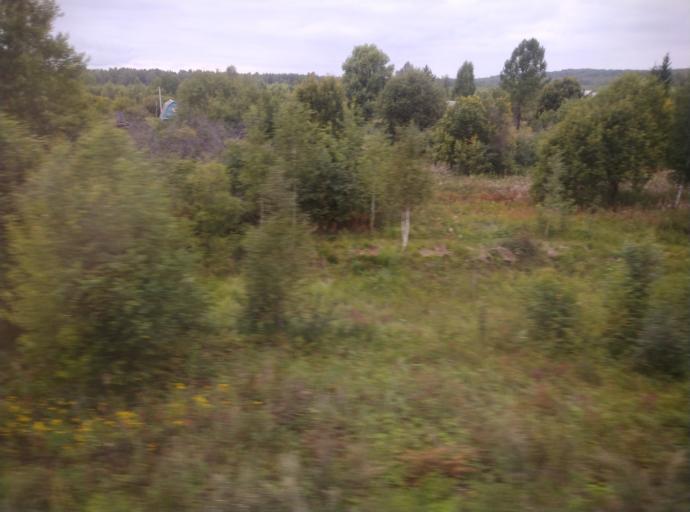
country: RU
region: Kostroma
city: Kosmynino
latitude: 57.5949
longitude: 40.7727
